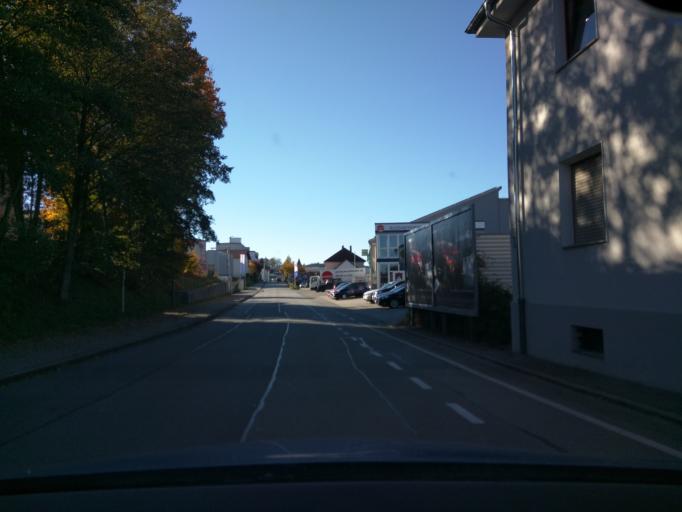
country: DE
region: Bavaria
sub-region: Lower Bavaria
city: Passau
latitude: 48.5722
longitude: 13.4317
